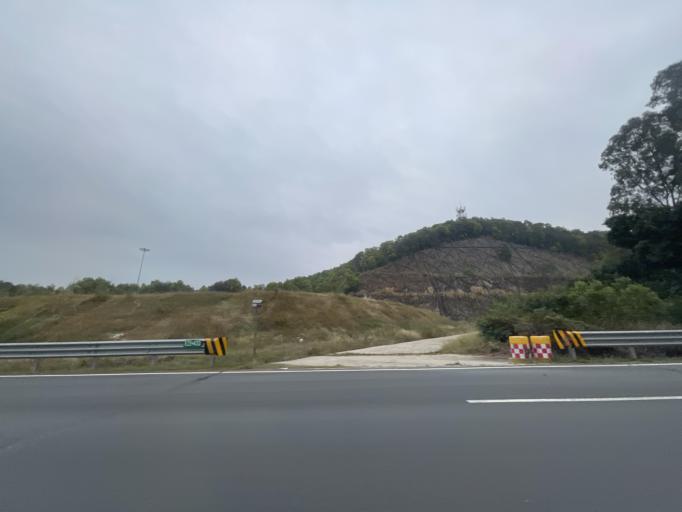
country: CN
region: Guangdong
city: Xinwan
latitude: 22.8076
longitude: 113.6395
